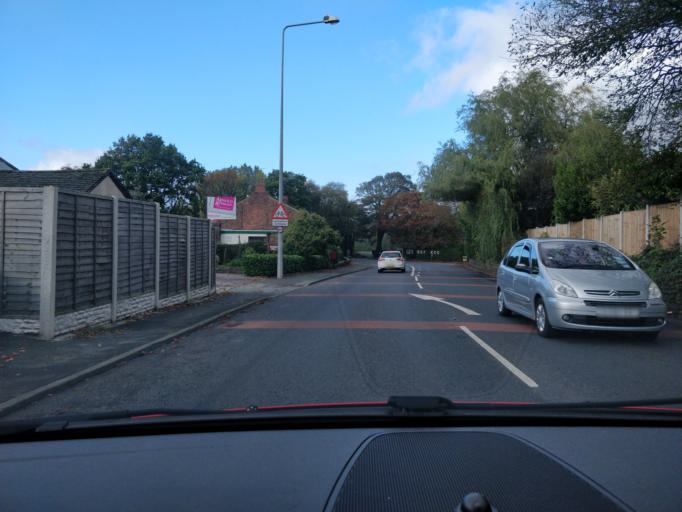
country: GB
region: England
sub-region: Lancashire
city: Ormskirk
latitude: 53.5961
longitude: -2.9225
